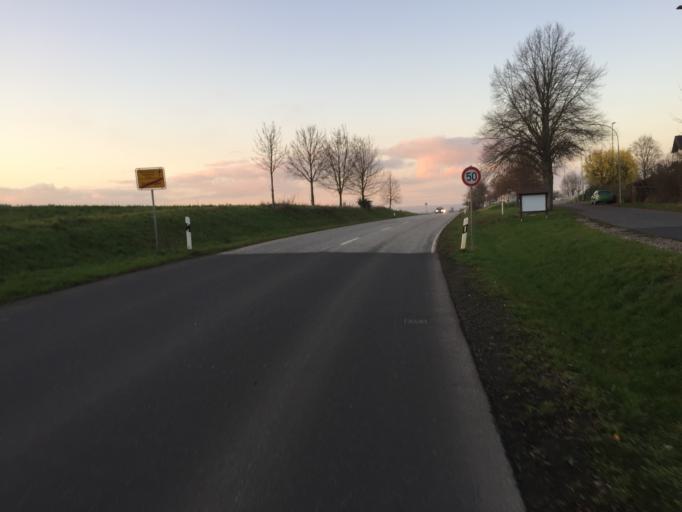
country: DE
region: Hesse
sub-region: Regierungsbezirk Giessen
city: Langgons
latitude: 50.5127
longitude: 8.7275
